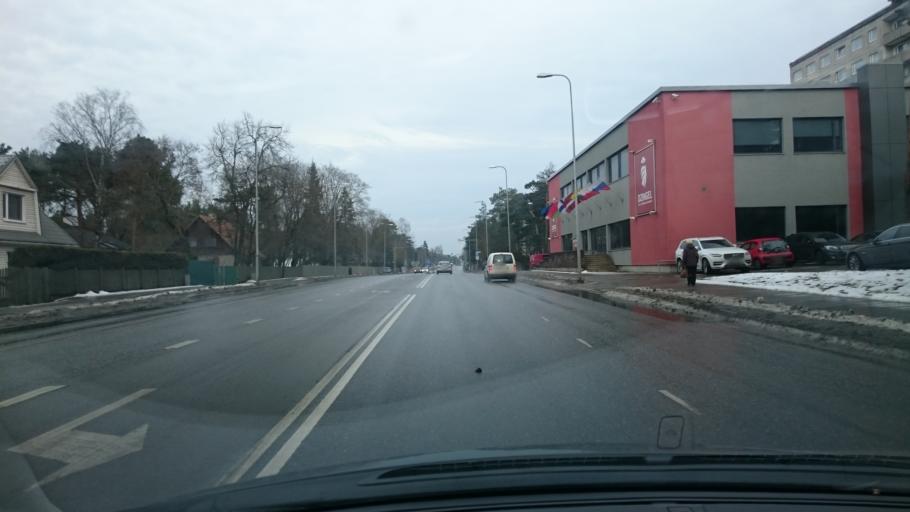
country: EE
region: Harju
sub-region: Tallinna linn
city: Tallinn
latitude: 59.3779
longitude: 24.7178
